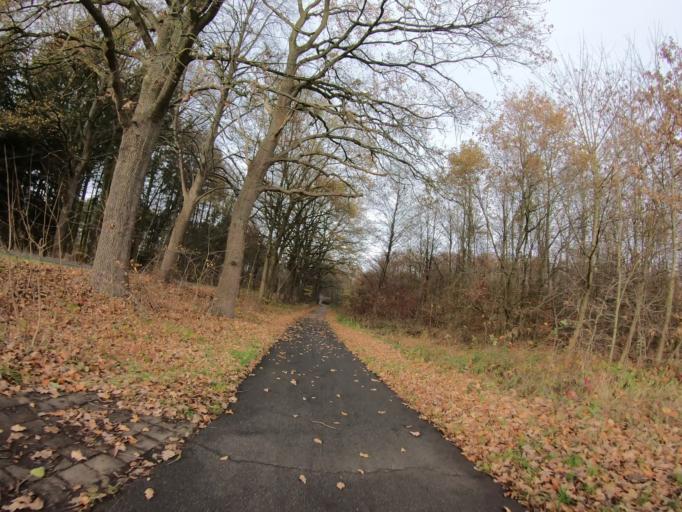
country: DE
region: Lower Saxony
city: Wagenhoff
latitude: 52.5397
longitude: 10.5200
